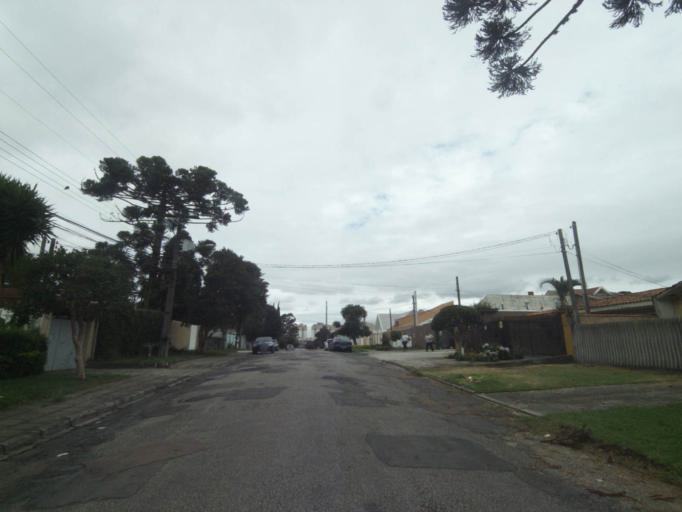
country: BR
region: Parana
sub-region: Curitiba
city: Curitiba
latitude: -25.4895
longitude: -49.2785
